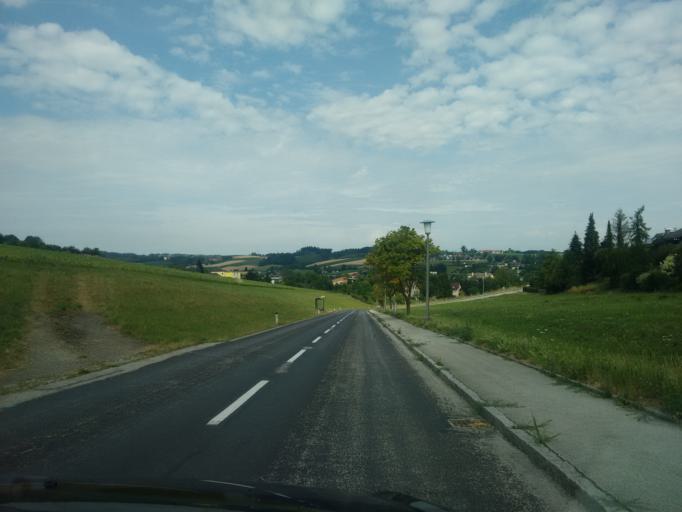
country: AT
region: Upper Austria
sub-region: Politischer Bezirk Grieskirchen
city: Grieskirchen
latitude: 48.2030
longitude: 13.8205
